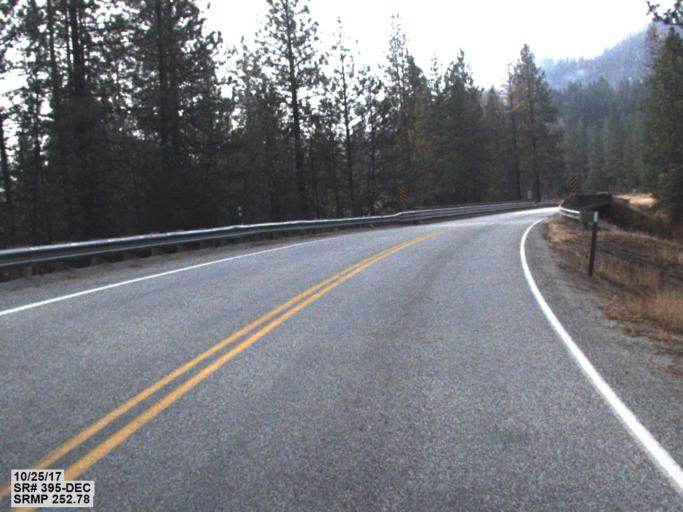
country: US
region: Washington
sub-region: Stevens County
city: Kettle Falls
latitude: 48.7754
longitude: -118.1419
